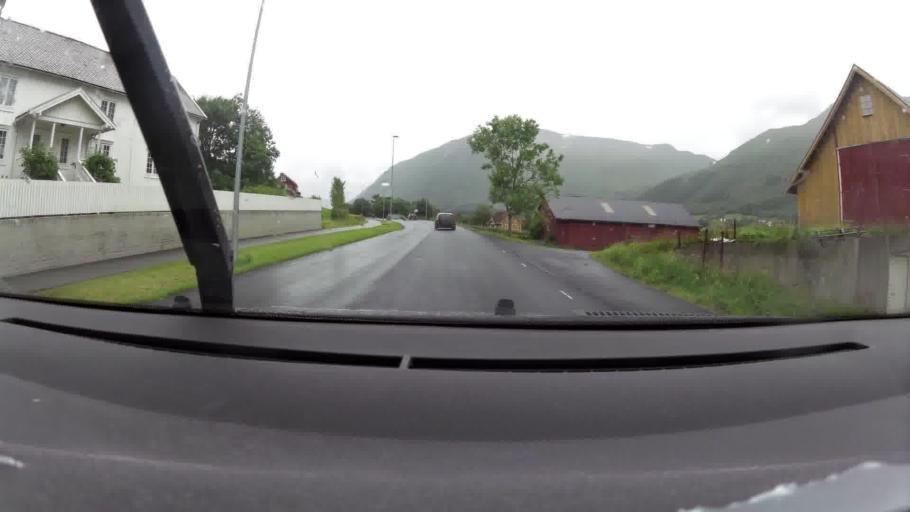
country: NO
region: More og Romsdal
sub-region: Gjemnes
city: Batnfjordsora
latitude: 62.8819
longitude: 7.6581
